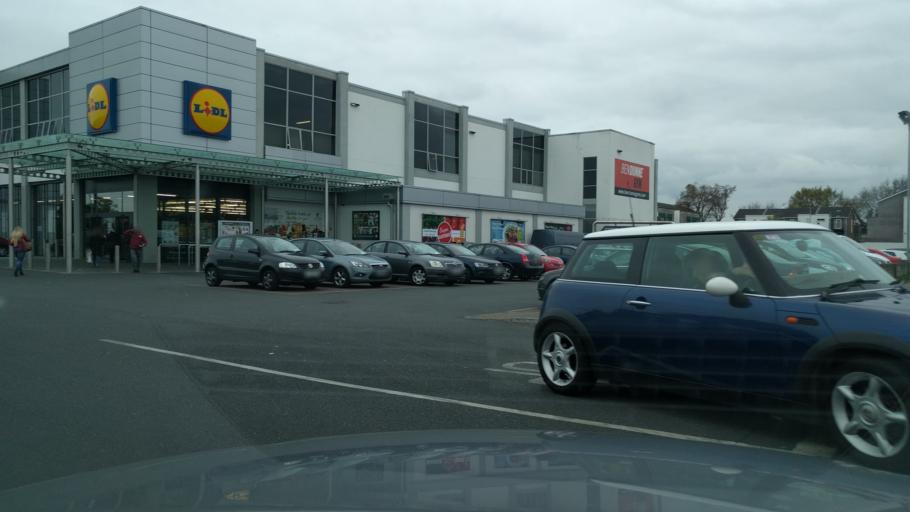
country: IE
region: Leinster
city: Lucan
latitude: 53.3477
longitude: -6.4231
